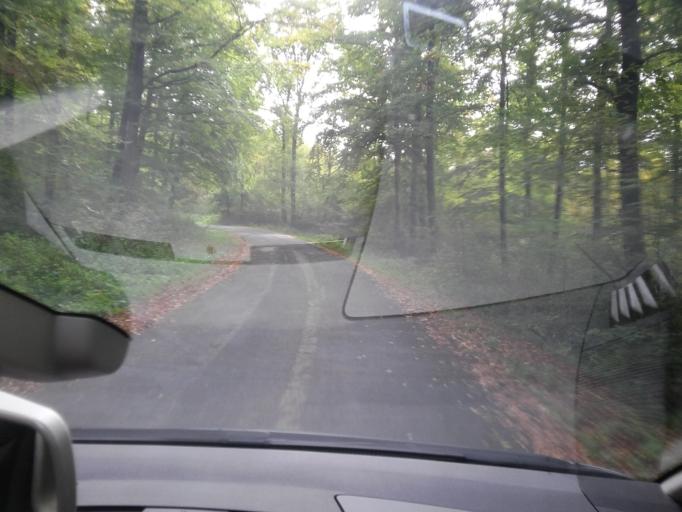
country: BE
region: Wallonia
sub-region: Province du Luxembourg
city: Attert
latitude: 49.7106
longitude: 5.7869
